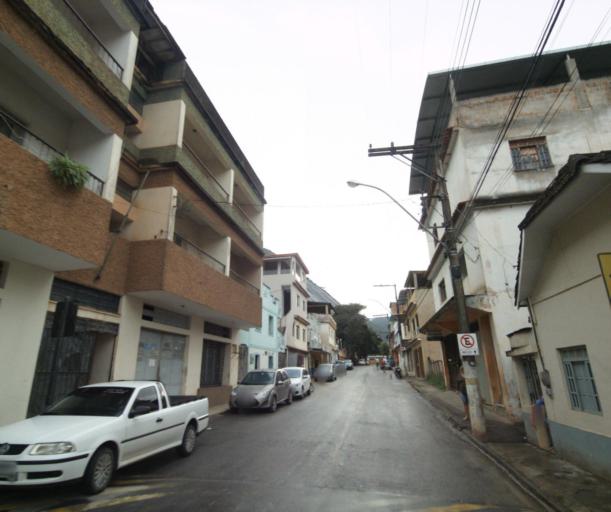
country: BR
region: Espirito Santo
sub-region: Muniz Freire
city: Muniz Freire
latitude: -20.4626
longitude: -41.4184
